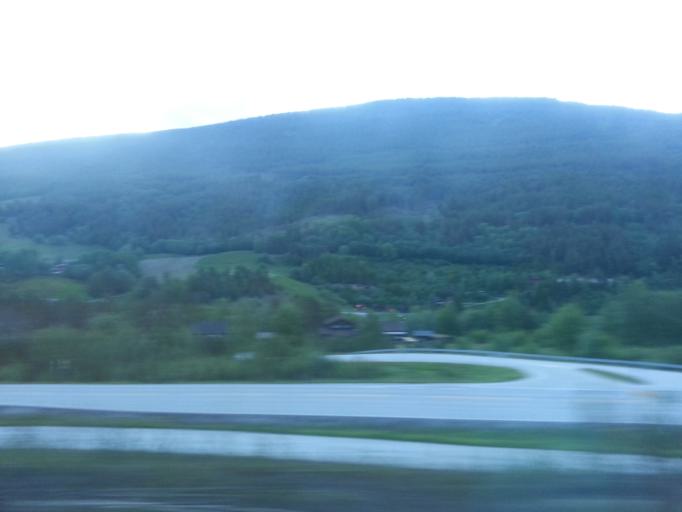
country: NO
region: Oppland
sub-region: Dovre
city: Dovre
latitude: 61.9168
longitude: 9.3541
